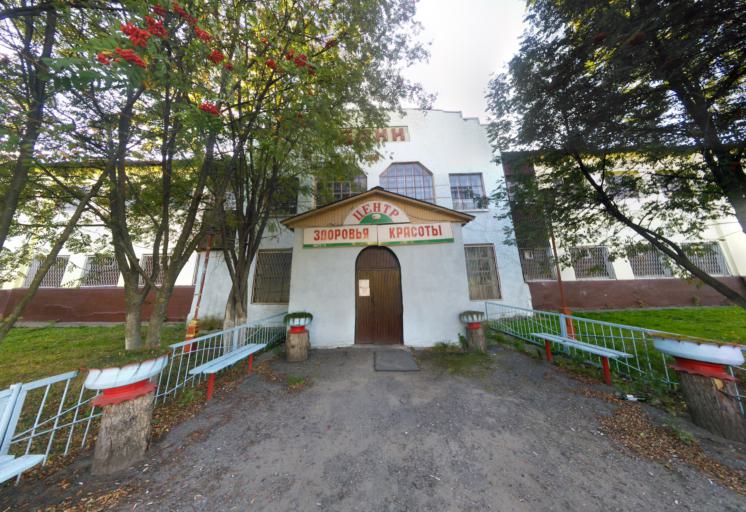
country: RU
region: Moskovskaya
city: Pavlovskiy Posad
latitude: 55.7849
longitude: 38.6486
